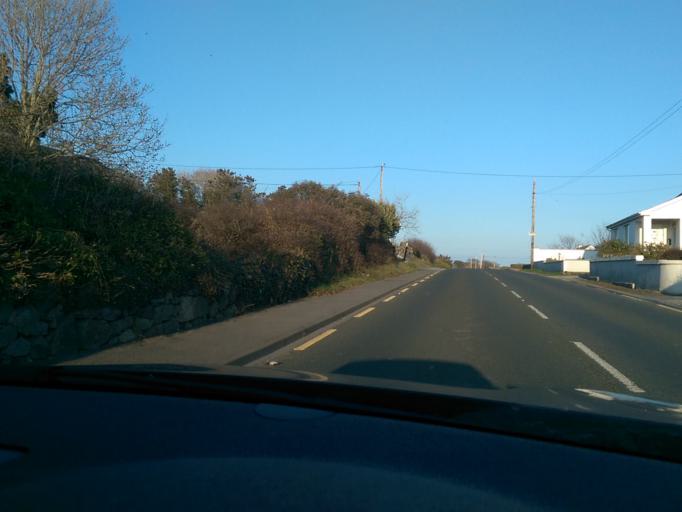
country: IE
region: Connaught
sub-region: County Galway
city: Oughterard
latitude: 53.2440
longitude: -9.3256
